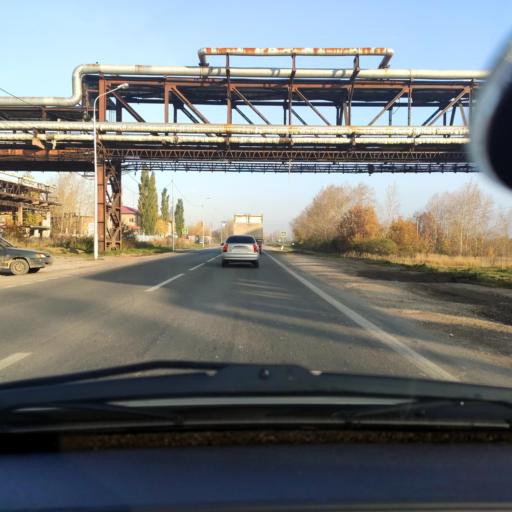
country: RU
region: Bashkortostan
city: Ufa
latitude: 54.8455
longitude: 56.1203
